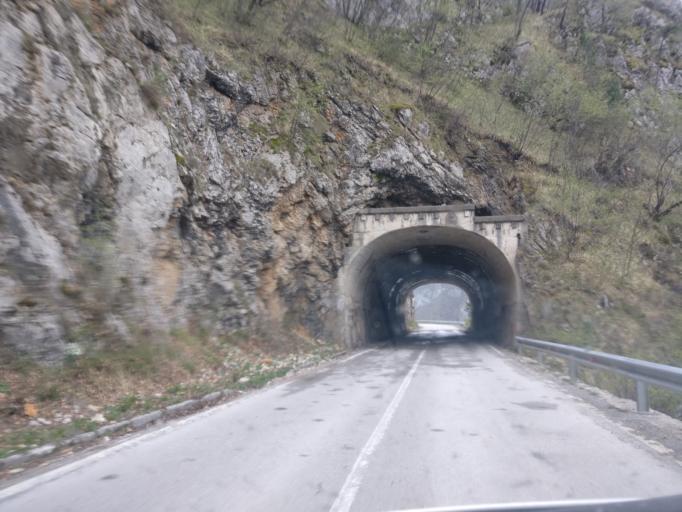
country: ME
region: Opstina Pluzine
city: Pluzine
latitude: 43.2489
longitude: 18.8330
